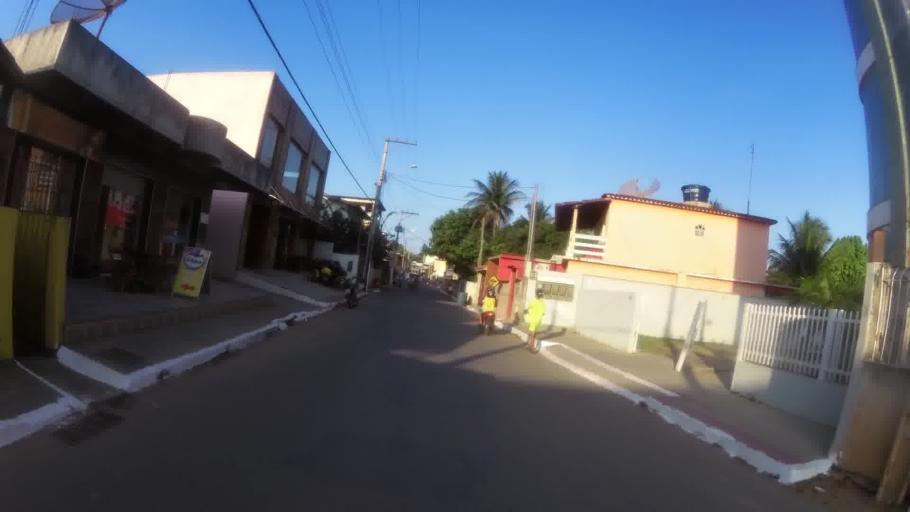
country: BR
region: Espirito Santo
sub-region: Piuma
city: Piuma
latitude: -20.8892
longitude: -40.7769
